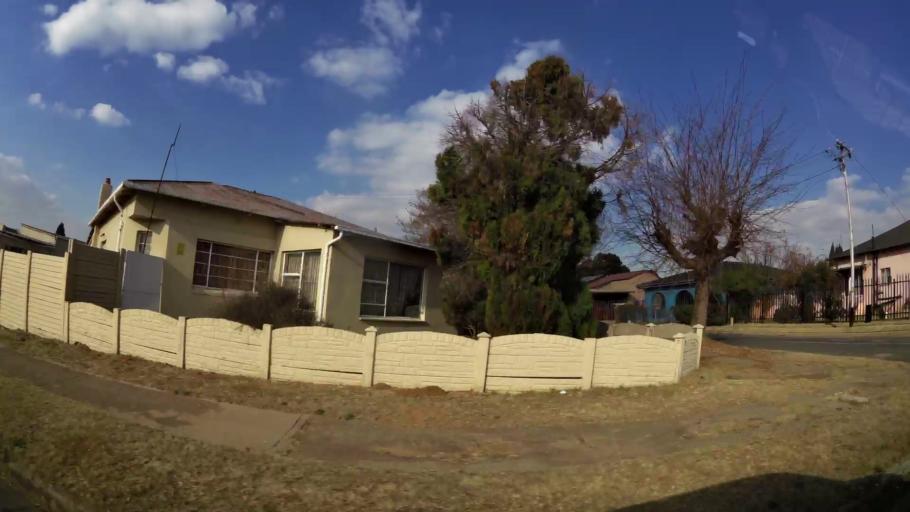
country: ZA
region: Gauteng
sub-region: West Rand District Municipality
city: Krugersdorp
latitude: -26.0951
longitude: 27.7436
